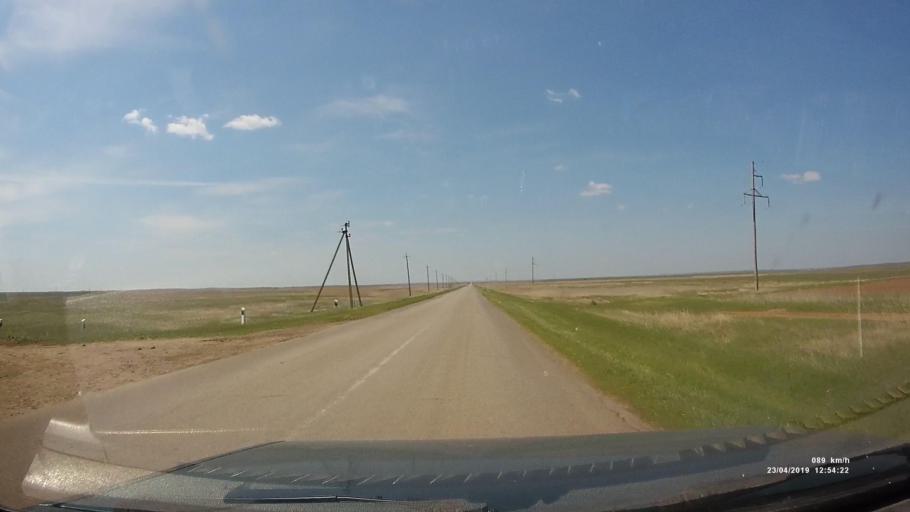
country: RU
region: Kalmykiya
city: Yashalta
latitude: 46.5796
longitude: 42.5798
